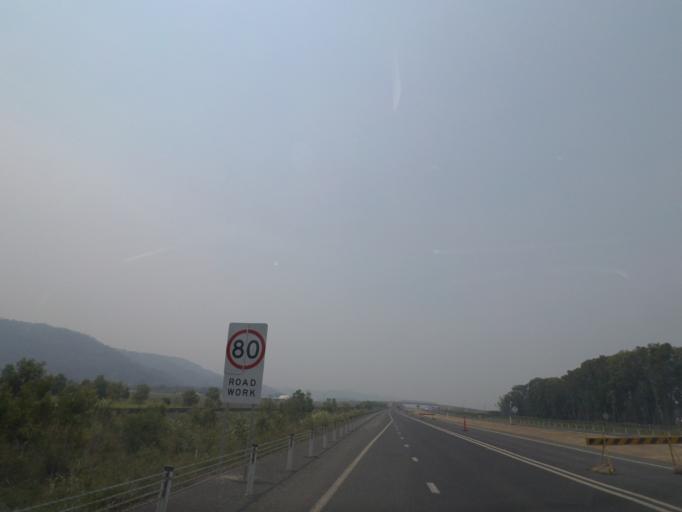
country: AU
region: New South Wales
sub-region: Ballina
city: Ballina
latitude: -28.9071
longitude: 153.4788
